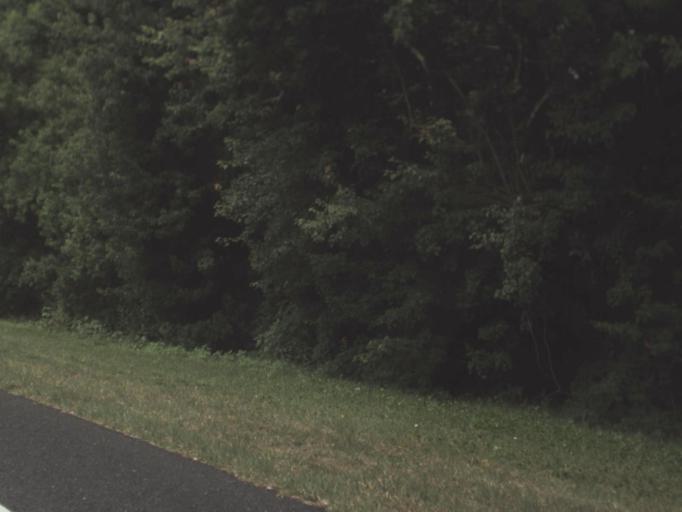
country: US
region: Florida
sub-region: Clay County
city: Orange Park
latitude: 30.1234
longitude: -81.7045
